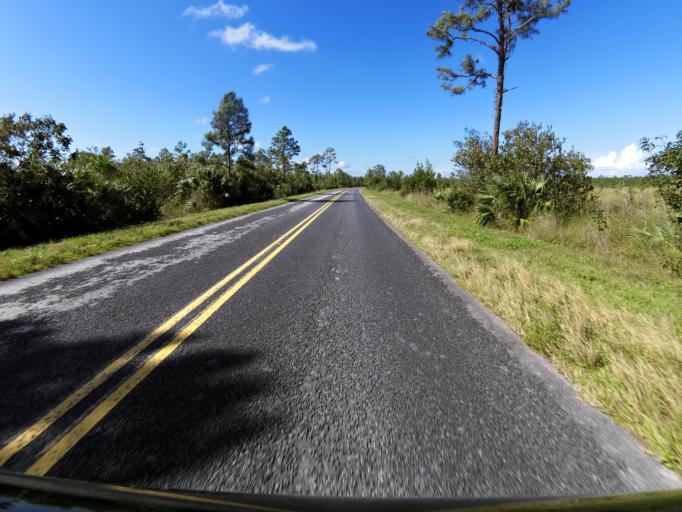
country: US
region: Florida
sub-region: Miami-Dade County
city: Florida City
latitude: 25.4186
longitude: -80.6712
